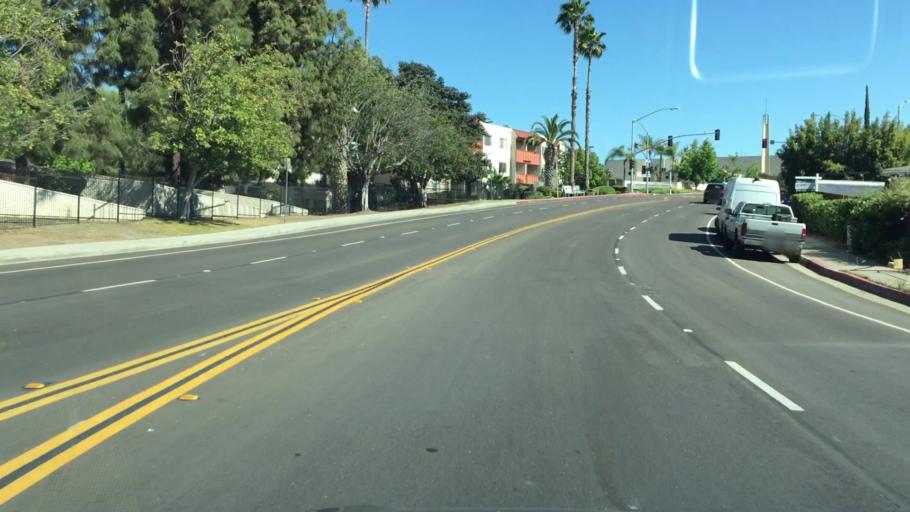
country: US
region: California
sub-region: San Diego County
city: Lemon Grove
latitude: 32.7663
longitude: -117.0672
